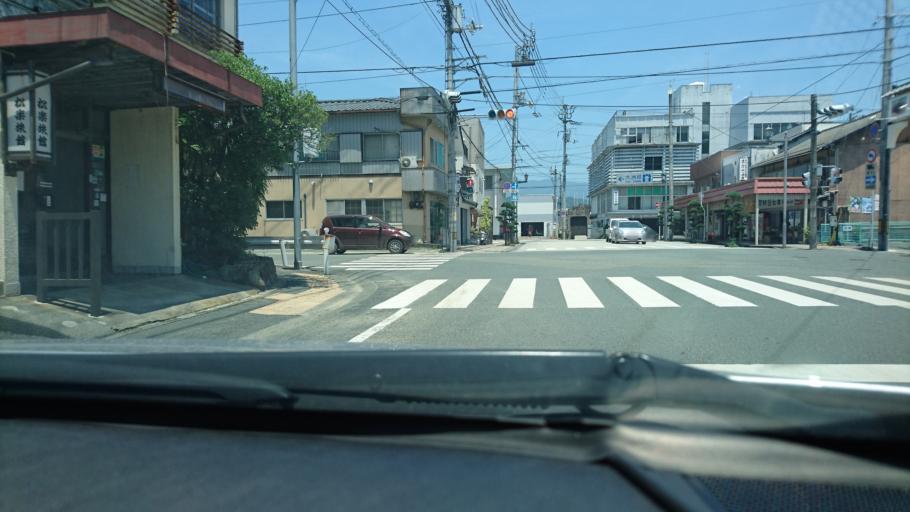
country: JP
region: Ehime
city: Ozu
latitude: 33.5074
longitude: 132.5427
